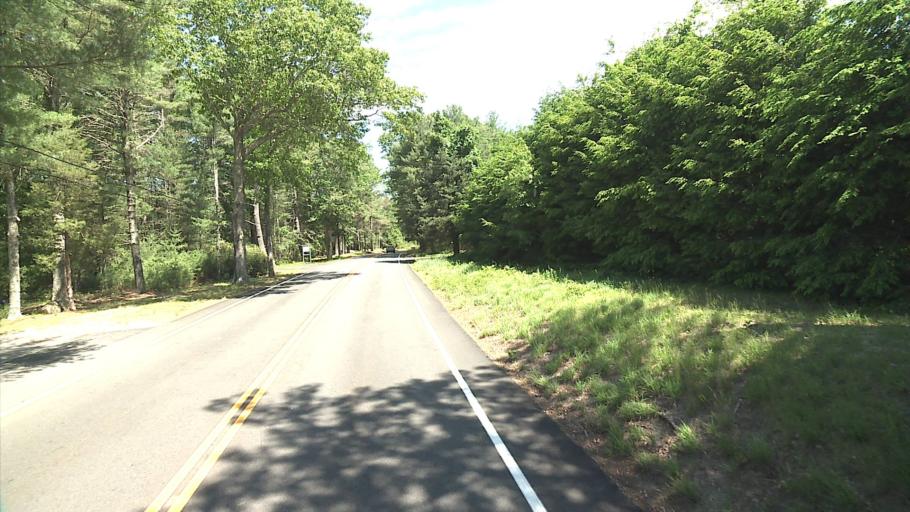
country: US
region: Connecticut
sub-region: Windham County
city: Plainfield
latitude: 41.5963
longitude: -71.8554
